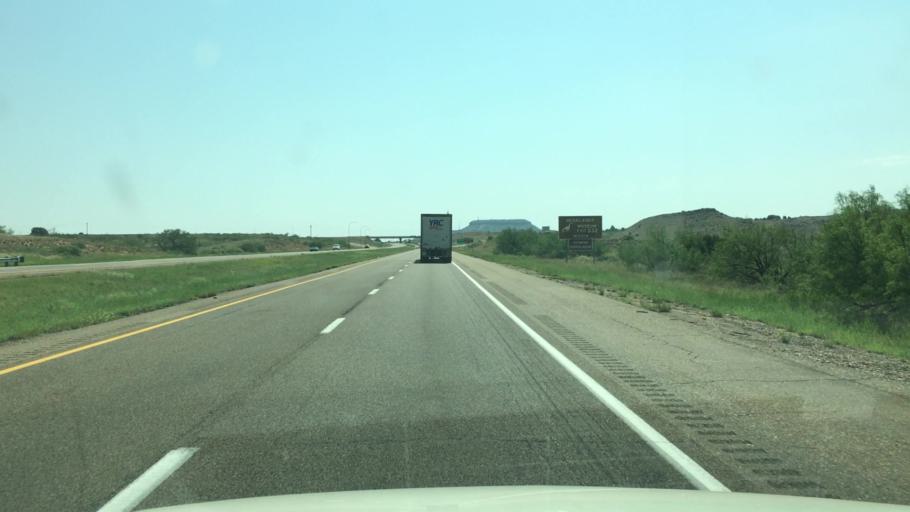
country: US
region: New Mexico
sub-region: Quay County
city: Tucumcari
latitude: 35.1549
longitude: -103.7557
